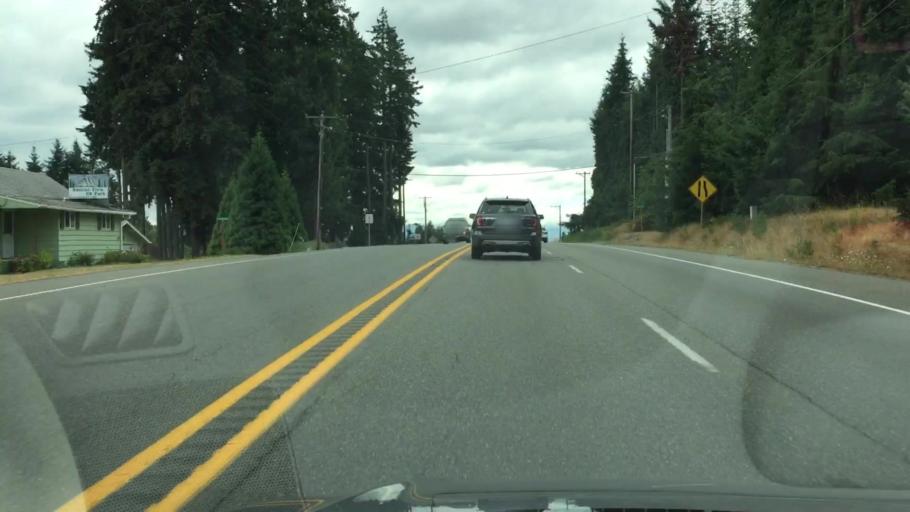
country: US
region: Washington
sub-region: Pierce County
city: Graham
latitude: 47.0292
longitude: -122.2961
